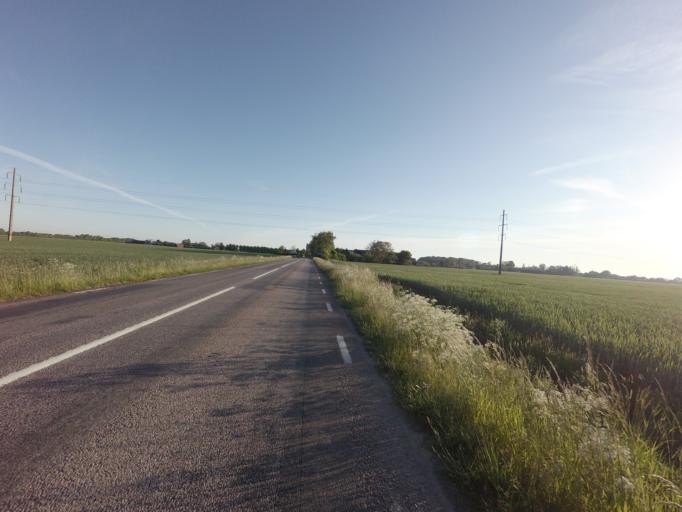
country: SE
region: Skane
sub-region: Helsingborg
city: Odakra
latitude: 56.1710
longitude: 12.6789
